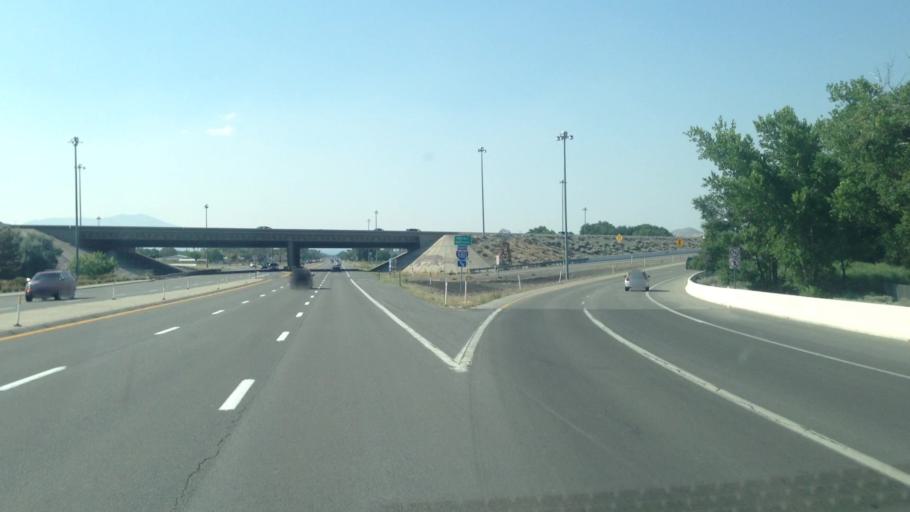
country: US
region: Nevada
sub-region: Washoe County
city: Sparks
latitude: 39.4073
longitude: -119.7489
